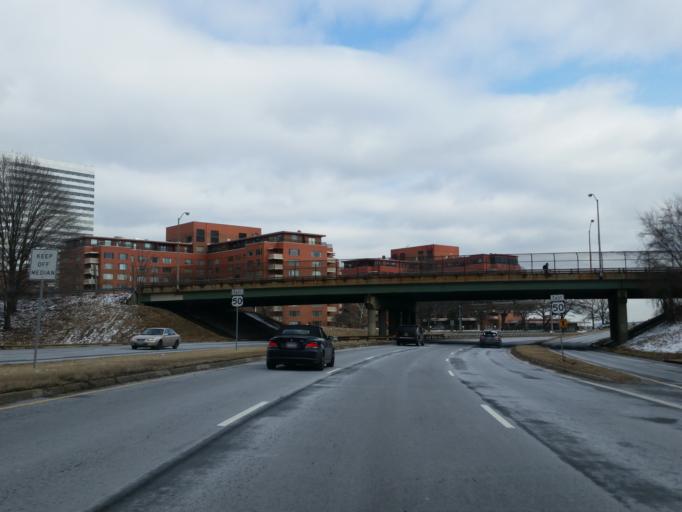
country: US
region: Virginia
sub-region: Arlington County
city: Arlington
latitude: 38.8920
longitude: -77.0726
